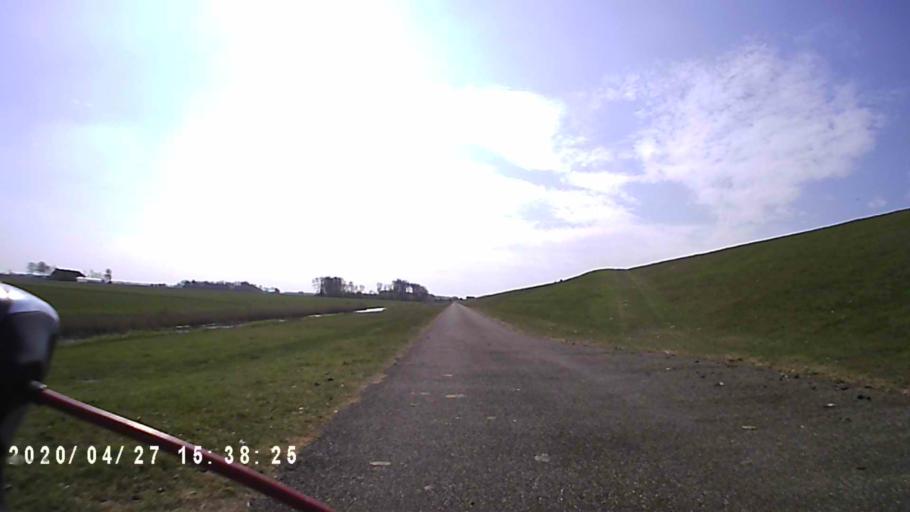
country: NL
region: Groningen
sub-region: Gemeente De Marne
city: Ulrum
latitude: 53.3947
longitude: 6.3180
